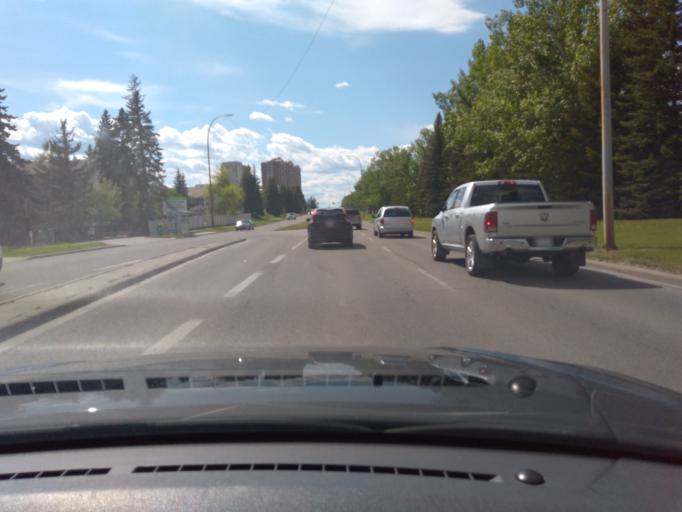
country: CA
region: Alberta
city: Calgary
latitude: 50.9723
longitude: -114.1015
